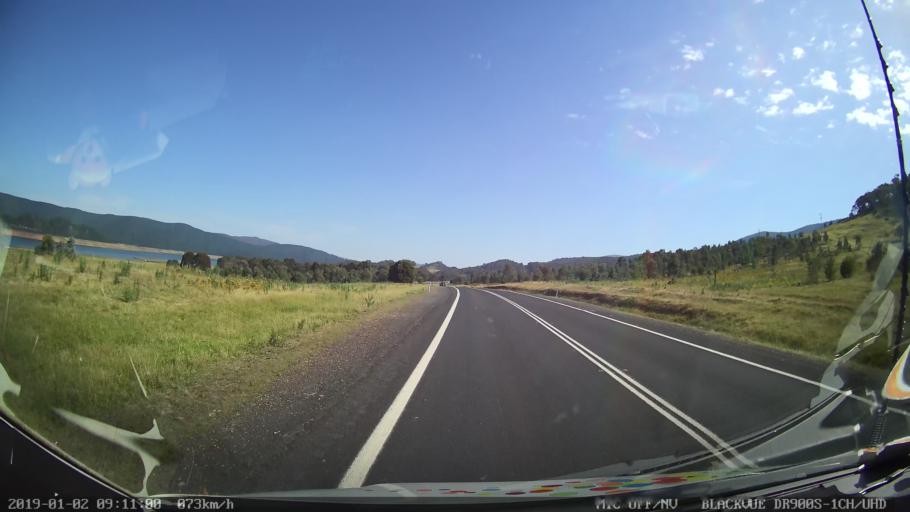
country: AU
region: New South Wales
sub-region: Tumut Shire
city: Tumut
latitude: -35.5159
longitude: 148.2688
